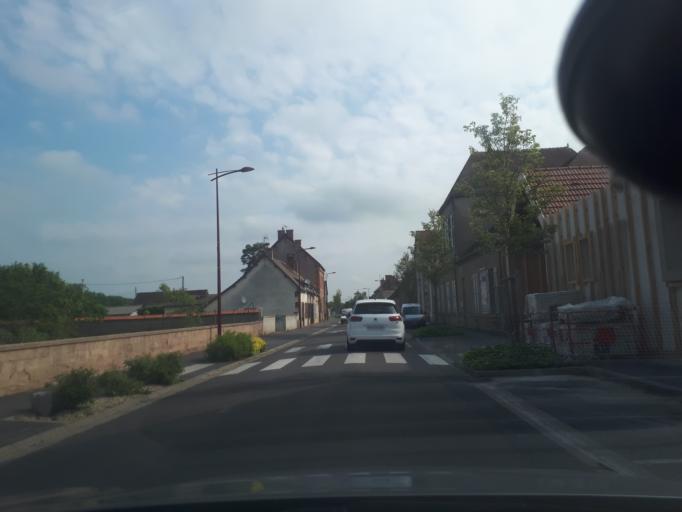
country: FR
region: Auvergne
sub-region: Departement de l'Allier
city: Dompierre-sur-Besbre
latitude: 46.4476
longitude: 3.6311
